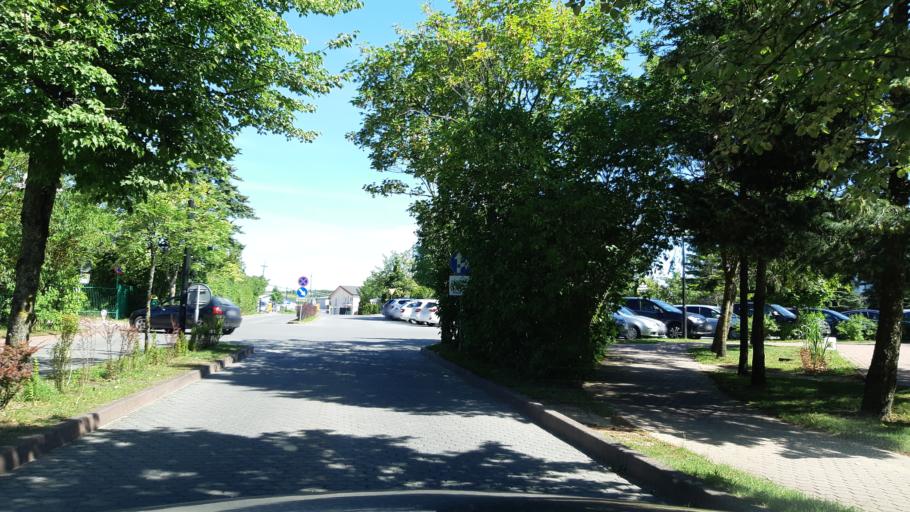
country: PL
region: Warmian-Masurian Voivodeship
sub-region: Powiat mragowski
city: Mikolajki
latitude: 53.8040
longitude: 21.5562
